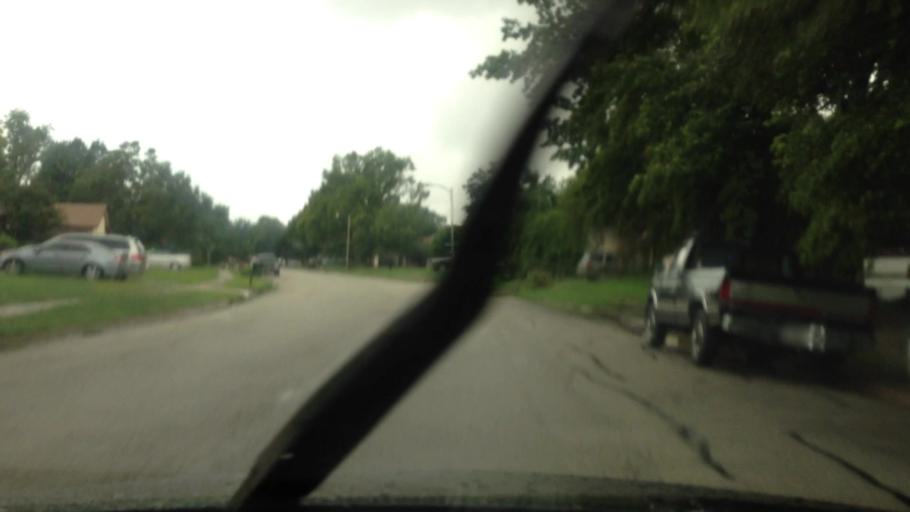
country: US
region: Texas
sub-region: Tarrant County
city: Colleyville
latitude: 32.8813
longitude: -97.2015
